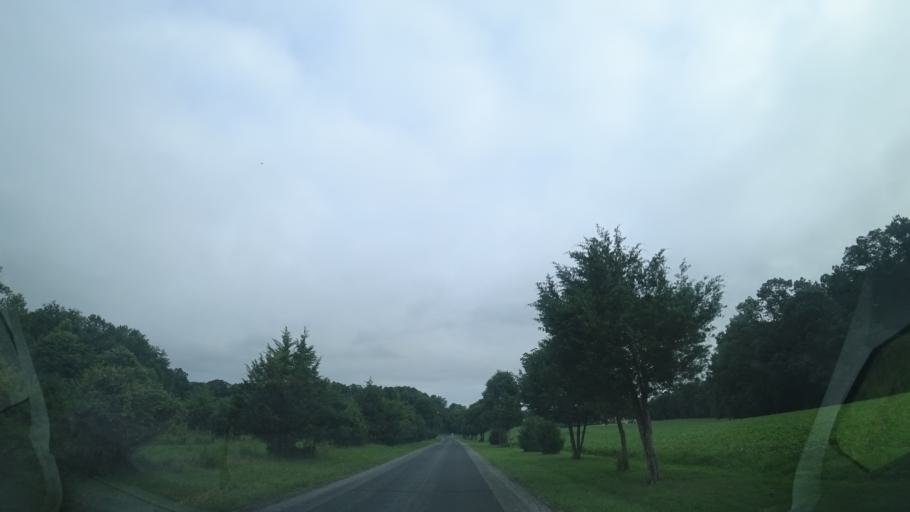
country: US
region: Maryland
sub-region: Montgomery County
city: Poolesville
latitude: 39.1139
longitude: -77.4553
